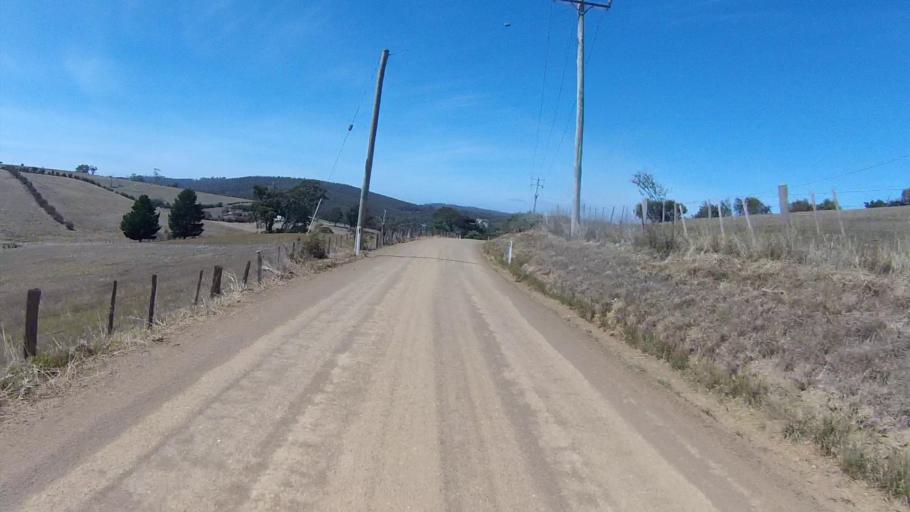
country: AU
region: Tasmania
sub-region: Sorell
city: Sorell
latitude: -42.7927
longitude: 147.6389
